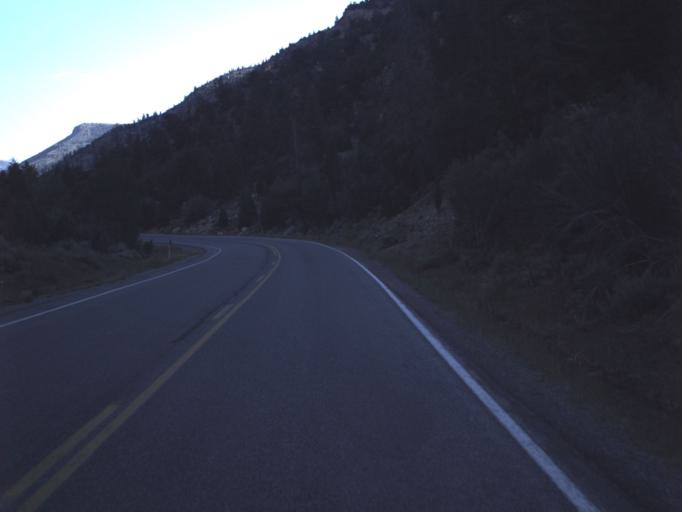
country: US
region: Utah
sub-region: Emery County
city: Huntington
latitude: 39.4324
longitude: -111.1301
